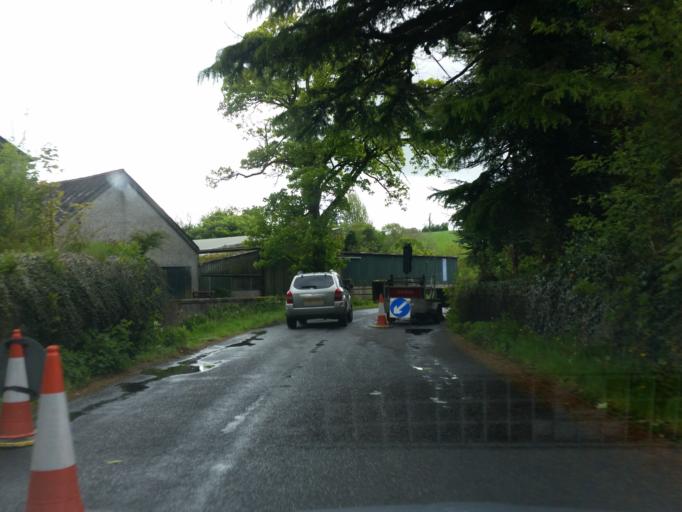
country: GB
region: Northern Ireland
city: Lisnaskea
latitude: 54.2443
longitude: -7.4297
